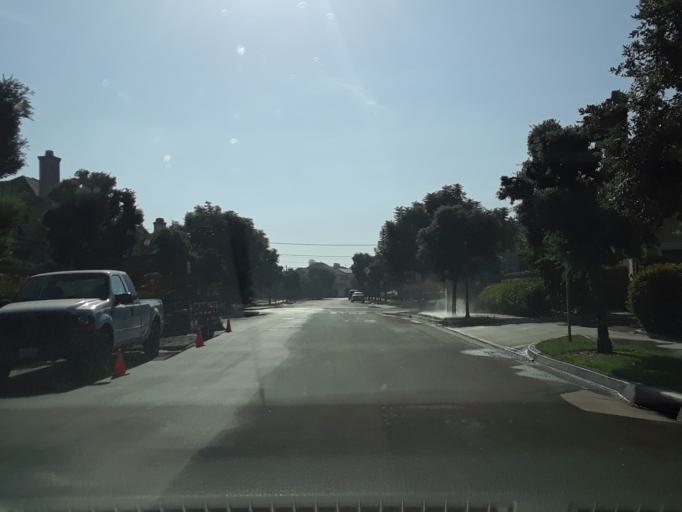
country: US
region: California
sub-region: Orange County
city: Irvine
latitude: 33.6961
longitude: -117.8129
